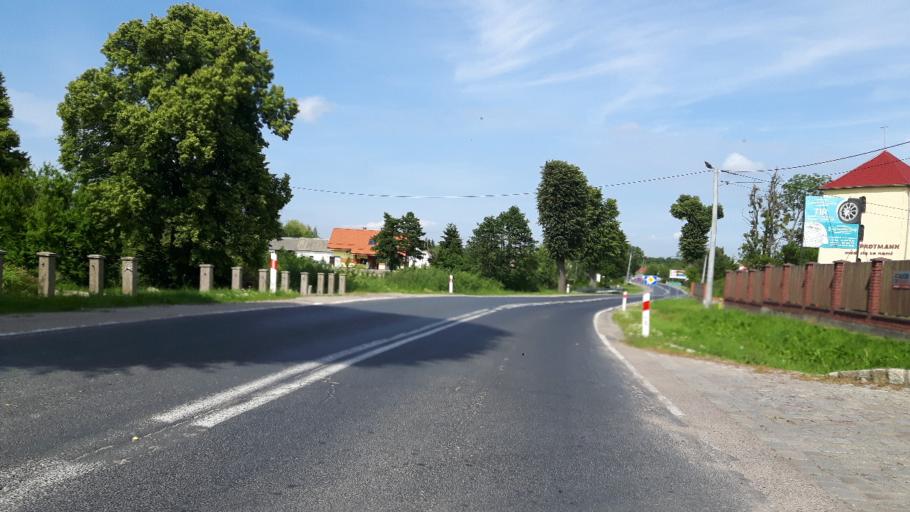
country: RU
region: Kaliningrad
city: Mamonovo
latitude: 54.4284
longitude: 19.8897
